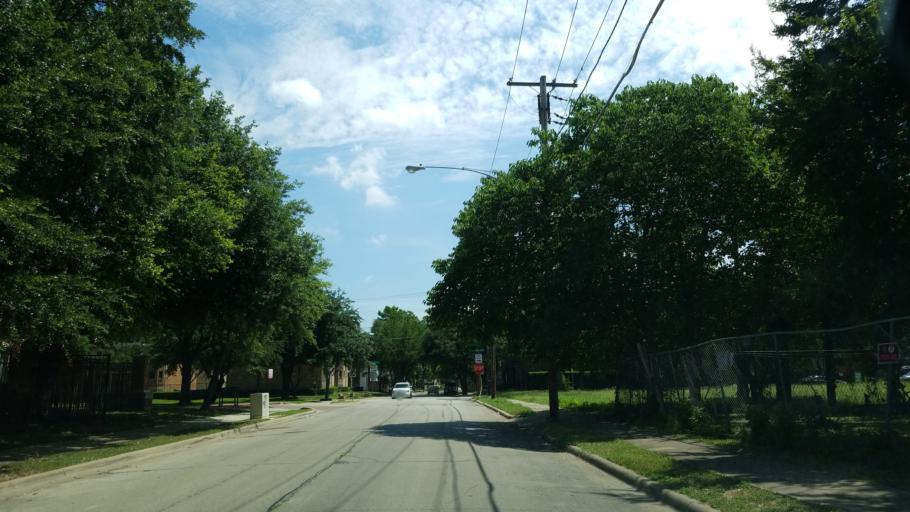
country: US
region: Texas
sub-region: Dallas County
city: Dallas
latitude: 32.8020
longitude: -96.7873
